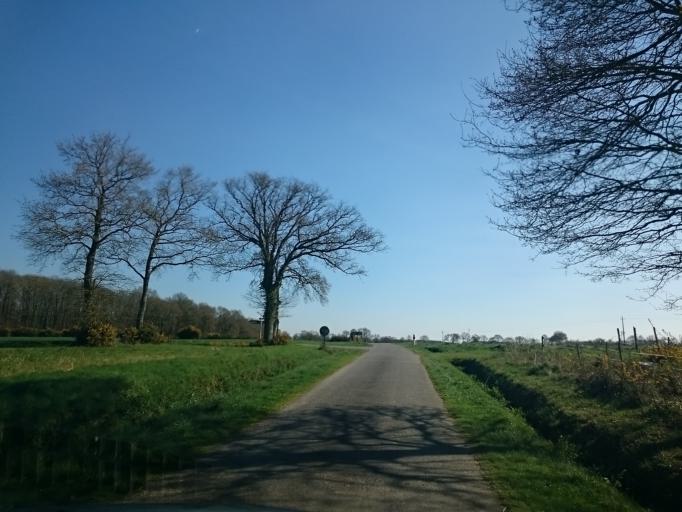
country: FR
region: Brittany
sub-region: Departement d'Ille-et-Vilaine
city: Chanteloup
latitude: 47.9523
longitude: -1.6420
